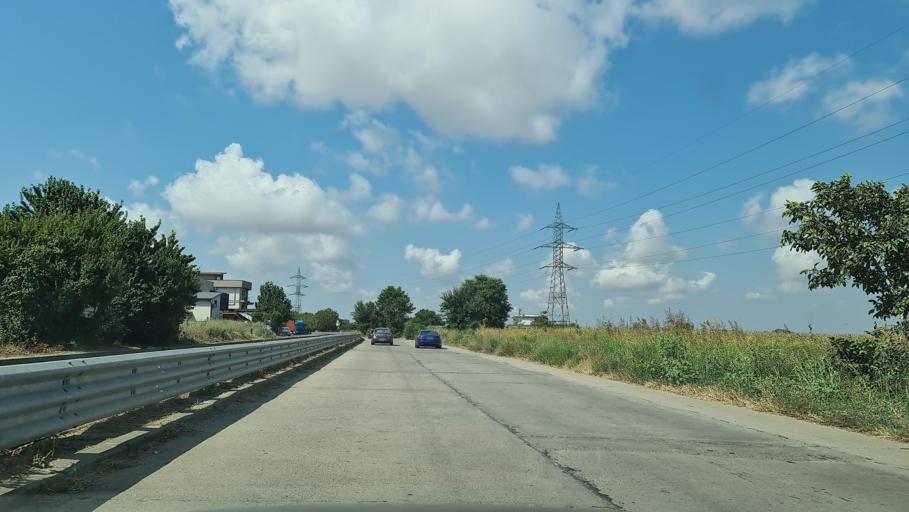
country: RO
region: Constanta
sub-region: Oras Eforie
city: Eforie Nord
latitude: 44.0768
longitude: 28.6313
